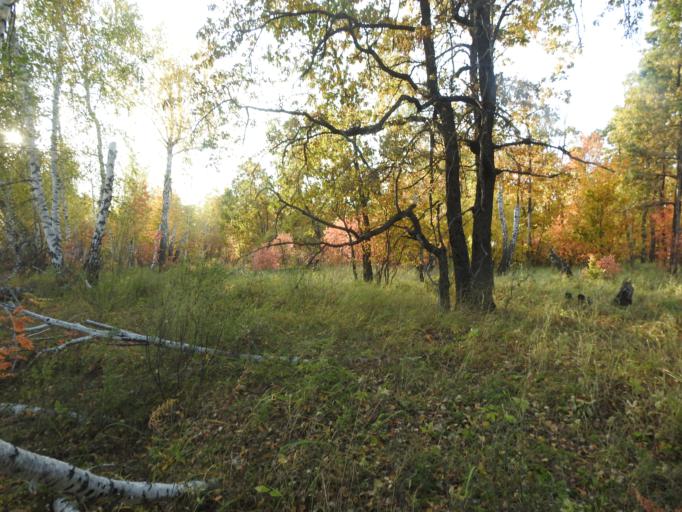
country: RU
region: Saratov
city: Baltay
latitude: 52.5014
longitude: 46.7560
